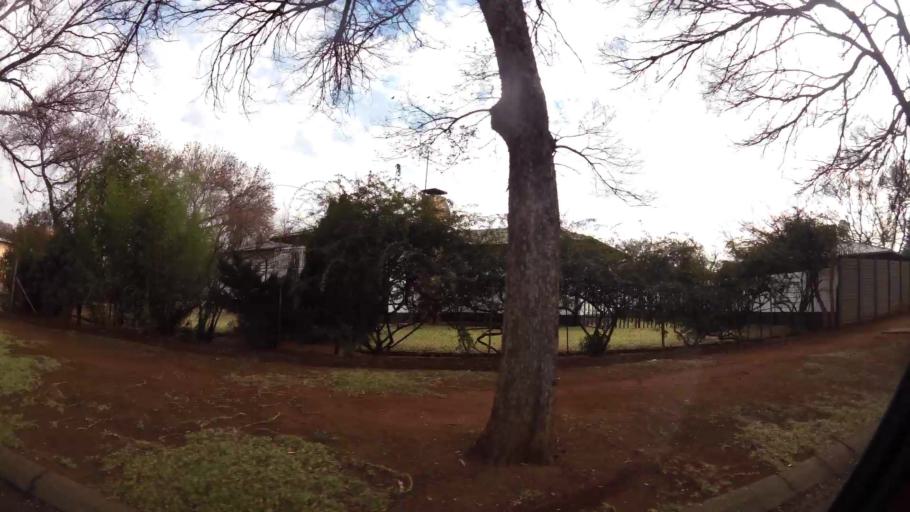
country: ZA
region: Gauteng
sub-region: Sedibeng District Municipality
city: Vanderbijlpark
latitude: -26.7021
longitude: 27.8294
